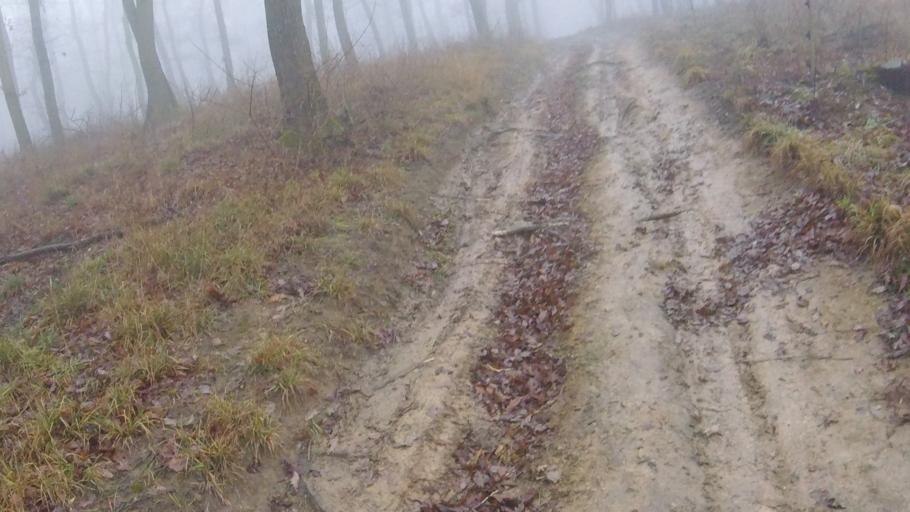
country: HU
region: Pest
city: Biatorbagy
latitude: 47.4462
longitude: 18.8490
